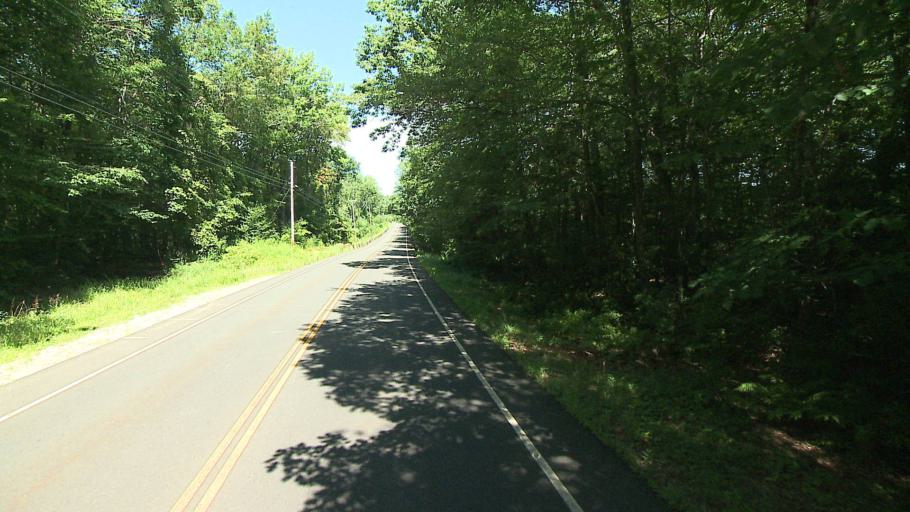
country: US
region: Connecticut
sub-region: Litchfield County
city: Winsted
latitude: 41.9919
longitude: -72.9827
